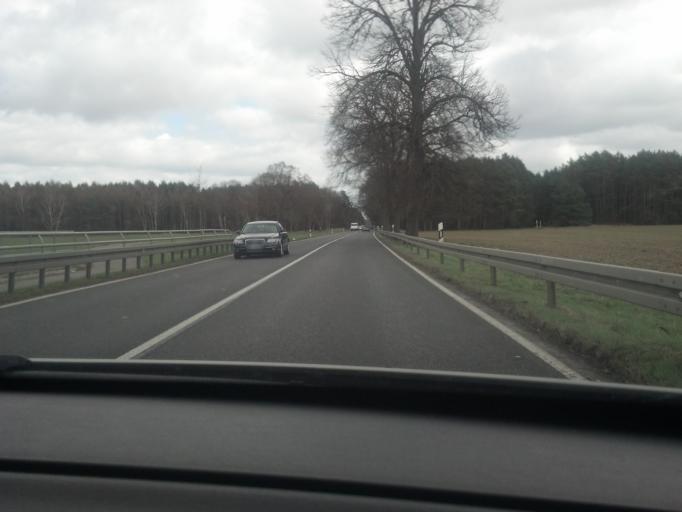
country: DE
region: Mecklenburg-Vorpommern
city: Wesenberg
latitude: 53.2723
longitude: 12.8421
